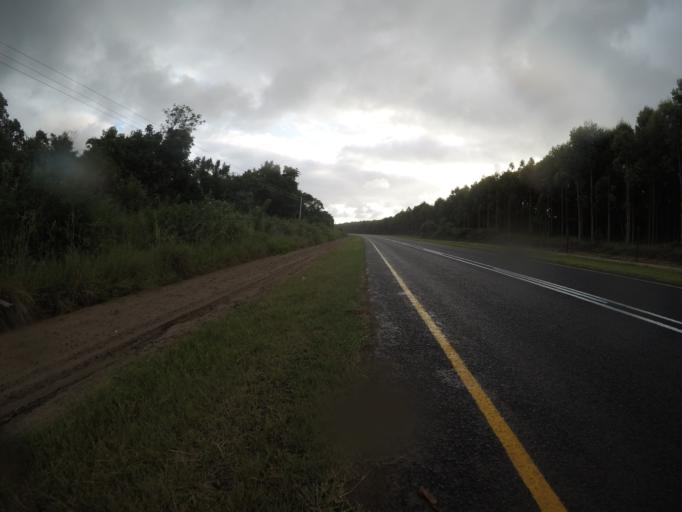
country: ZA
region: KwaZulu-Natal
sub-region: uMkhanyakude District Municipality
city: Mtubatuba
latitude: -28.3693
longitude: 32.2578
